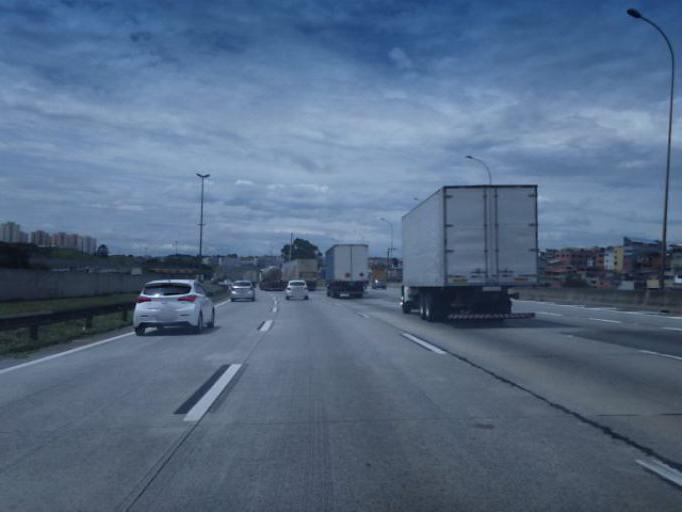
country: BR
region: Sao Paulo
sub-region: Carapicuiba
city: Carapicuiba
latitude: -23.5485
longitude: -46.8206
